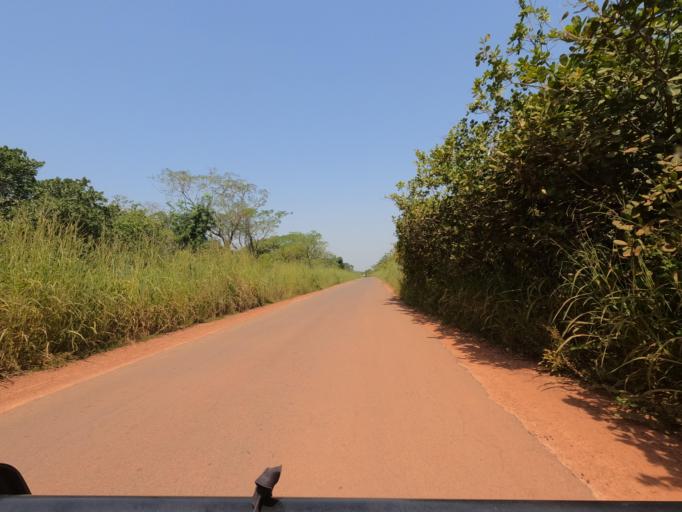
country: SN
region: Ziguinchor
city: Adeane
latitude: 12.3861
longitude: -15.7815
